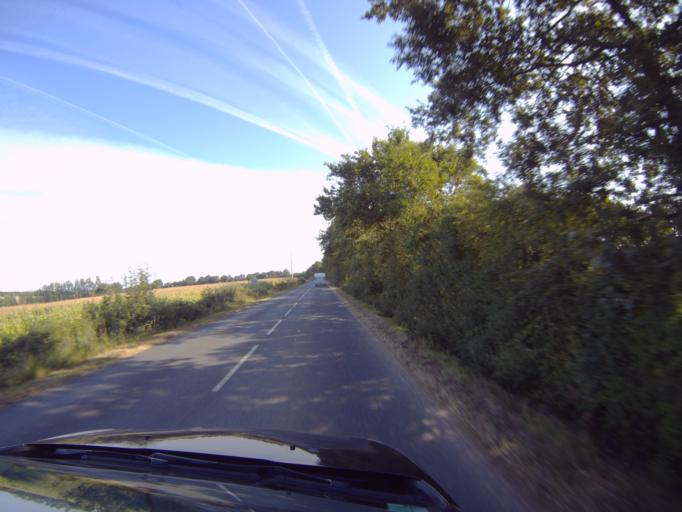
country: FR
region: Pays de la Loire
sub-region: Departement de la Vendee
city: Saint-Hilaire-de-Talmont
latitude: 46.4870
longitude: -1.5853
